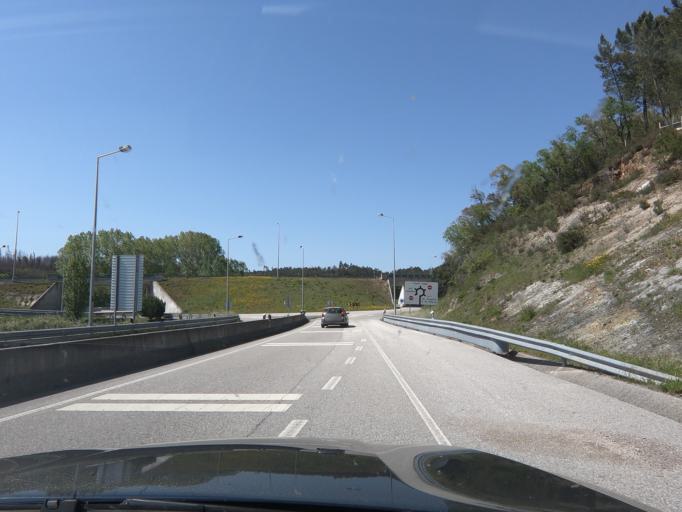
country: PT
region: Coimbra
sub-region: Vila Nova de Poiares
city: Poiares
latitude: 40.1749
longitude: -8.2678
